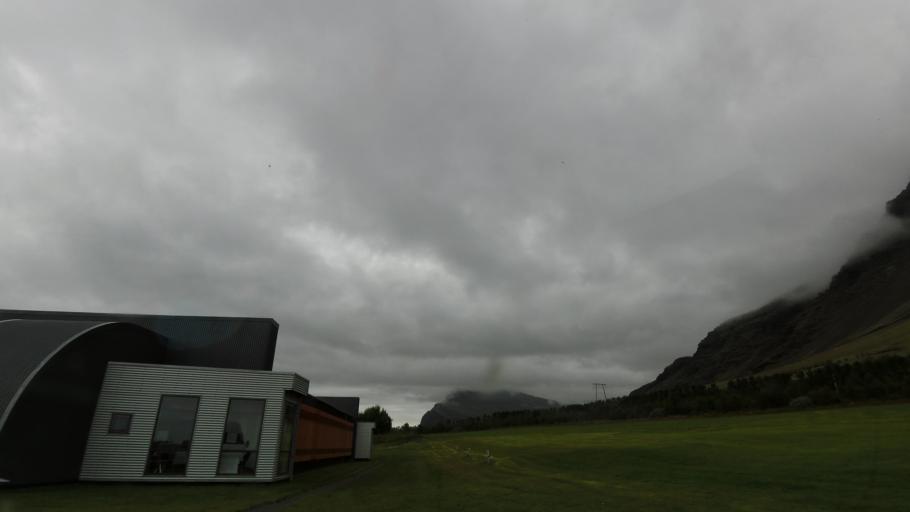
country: IS
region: East
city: Hoefn
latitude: 64.1299
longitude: -16.0168
